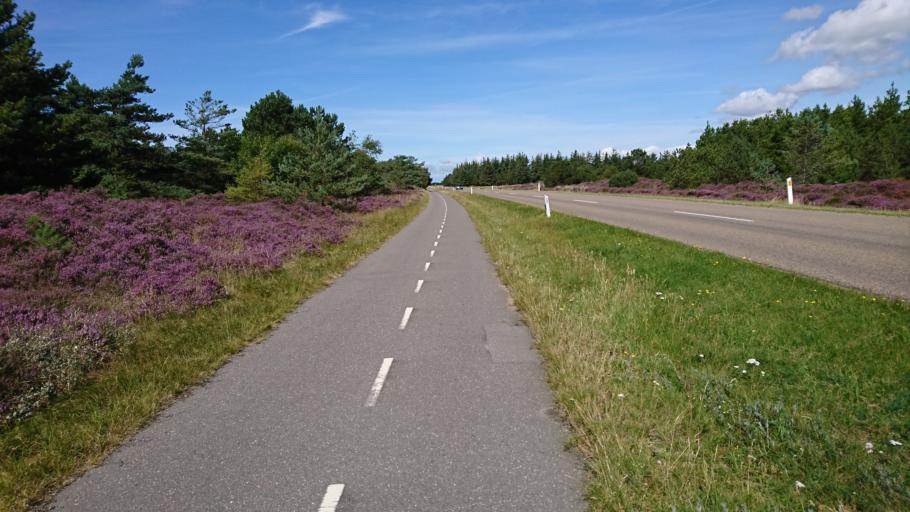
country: DK
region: South Denmark
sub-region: Fano Kommune
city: Nordby
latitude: 55.4052
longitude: 8.4180
